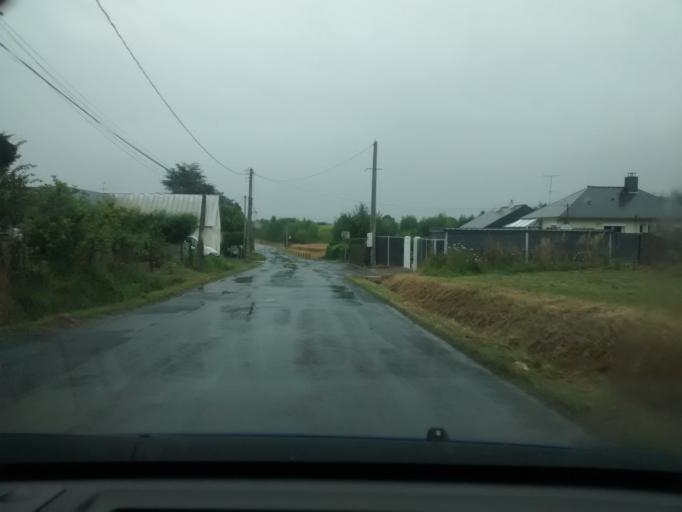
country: FR
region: Brittany
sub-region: Departement d'Ille-et-Vilaine
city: Betton
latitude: 48.1654
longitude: -1.6243
